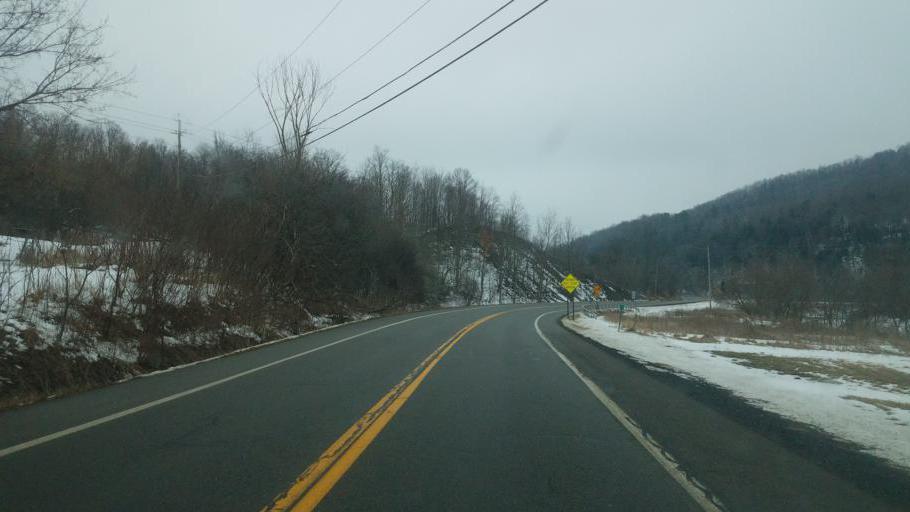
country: US
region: Pennsylvania
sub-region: Tioga County
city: Westfield
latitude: 42.0289
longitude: -77.5359
